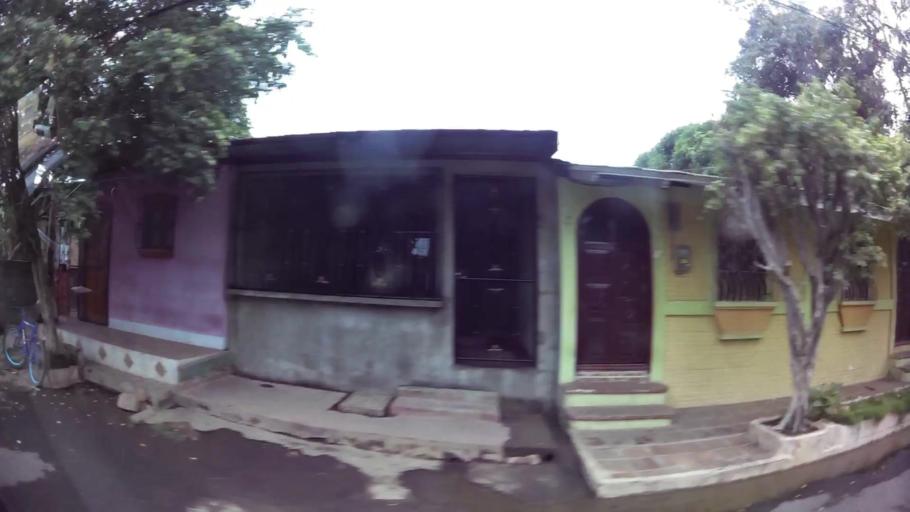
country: NI
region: Leon
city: Leon
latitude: 12.4488
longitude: -86.8722
